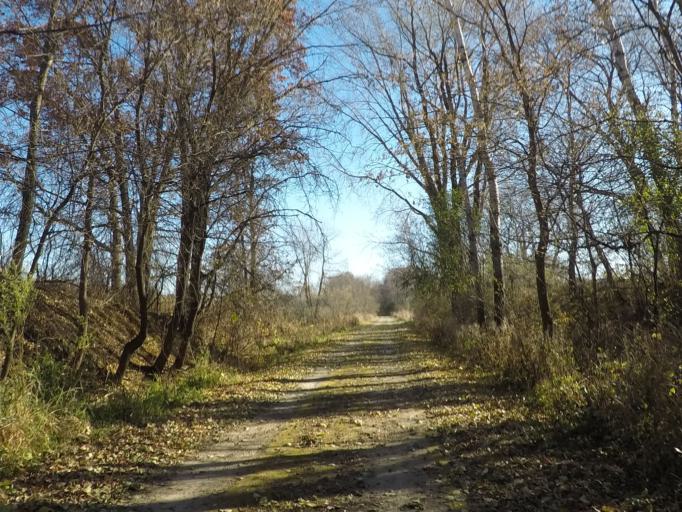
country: US
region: Wisconsin
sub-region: Jefferson County
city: Cambridge
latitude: 43.0434
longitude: -89.0276
